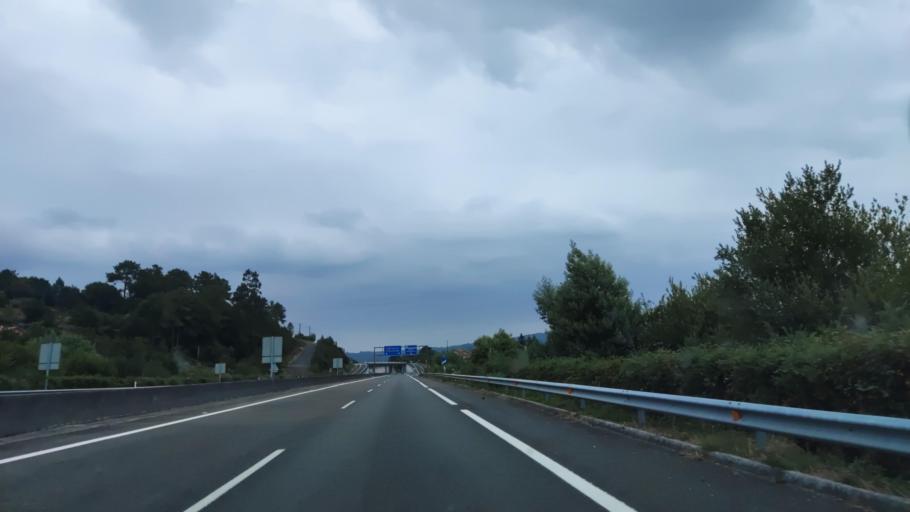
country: ES
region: Galicia
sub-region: Provincia da Coruna
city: Santiago de Compostela
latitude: 42.8213
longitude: -8.5325
